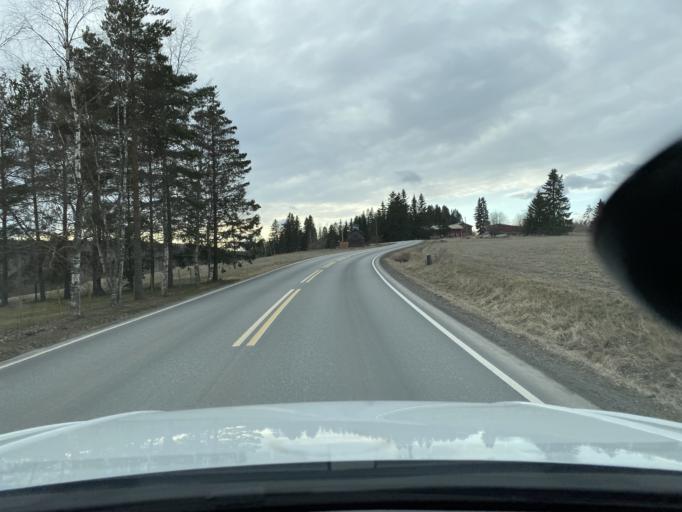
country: FI
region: Pirkanmaa
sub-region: Tampere
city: Vesilahti
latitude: 61.2891
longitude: 23.6091
